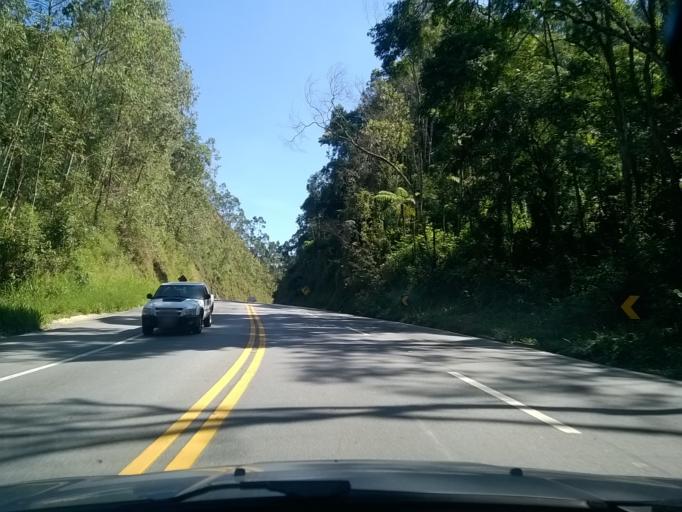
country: BR
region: Sao Paulo
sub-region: Francisco Morato
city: Francisco Morato
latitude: -23.2760
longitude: -46.8105
